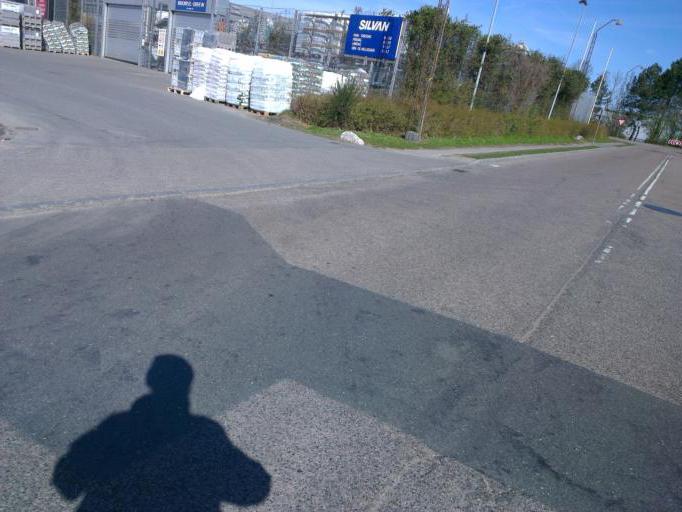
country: DK
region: Capital Region
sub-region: Frederikssund Kommune
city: Frederikssund
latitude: 55.8444
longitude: 12.0742
